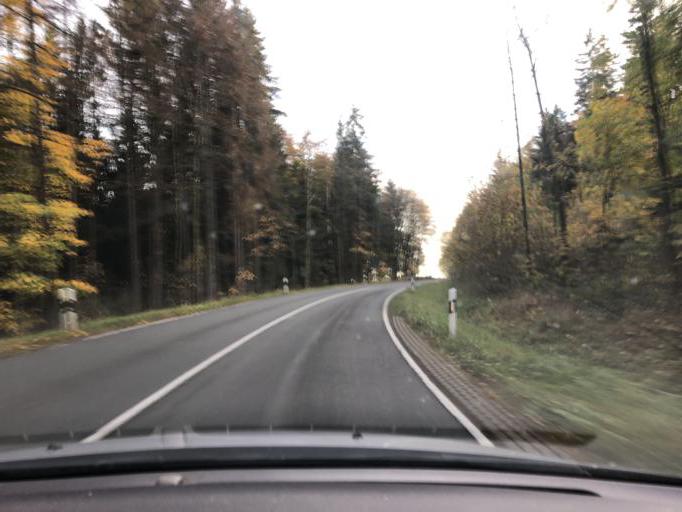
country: DE
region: Thuringia
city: Schleusingen
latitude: 50.4779
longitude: 10.7626
